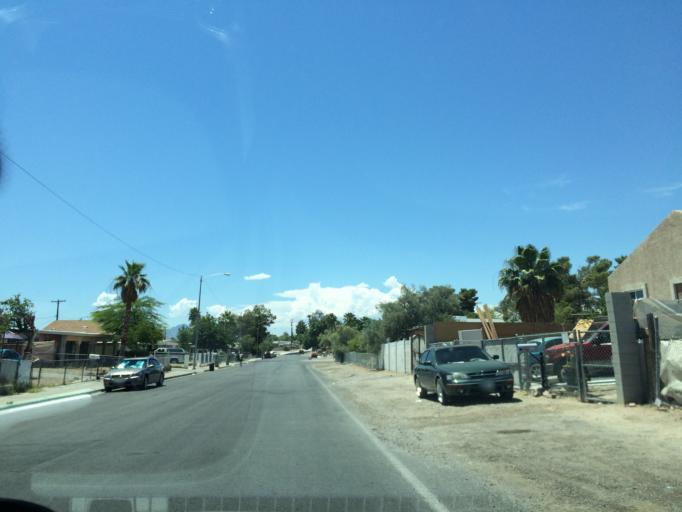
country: US
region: Nevada
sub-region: Clark County
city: Winchester
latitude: 36.1582
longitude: -115.0968
